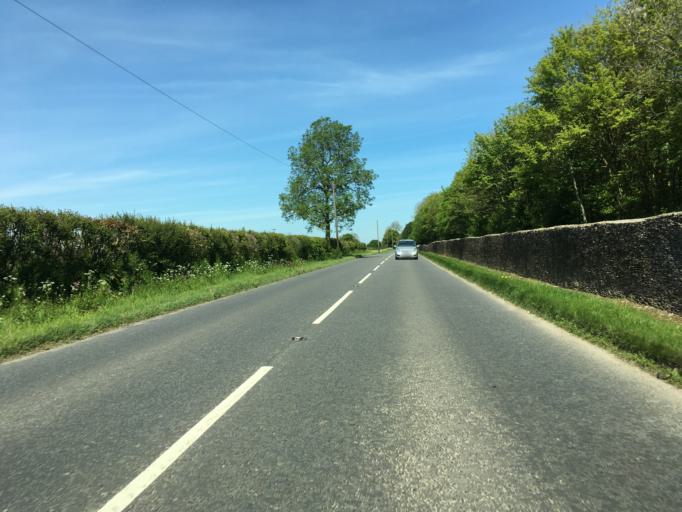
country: GB
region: England
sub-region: Wiltshire
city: Charlton
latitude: 51.6075
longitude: -2.0837
